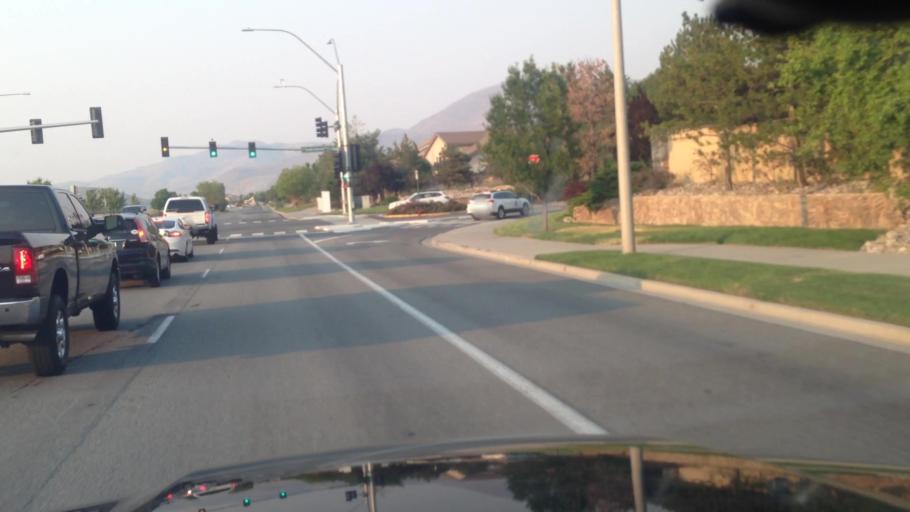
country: US
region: Nevada
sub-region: Washoe County
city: Sparks
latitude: 39.4431
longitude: -119.7460
